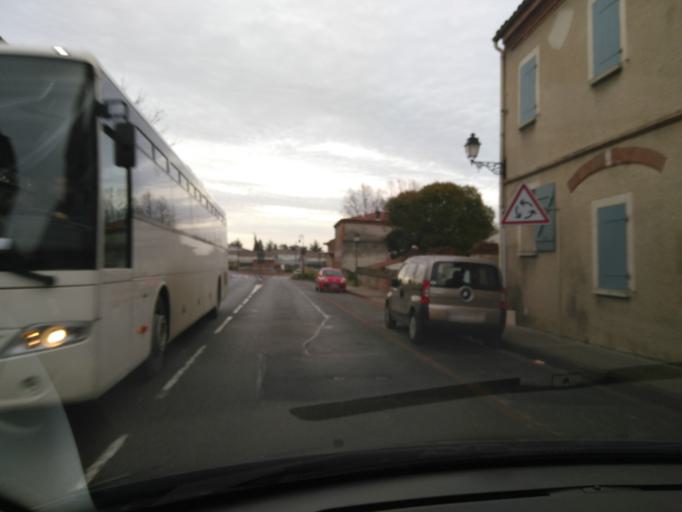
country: FR
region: Midi-Pyrenees
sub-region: Departement de la Haute-Garonne
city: Castelnau-d'Estretefonds
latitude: 43.7818
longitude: 1.3597
